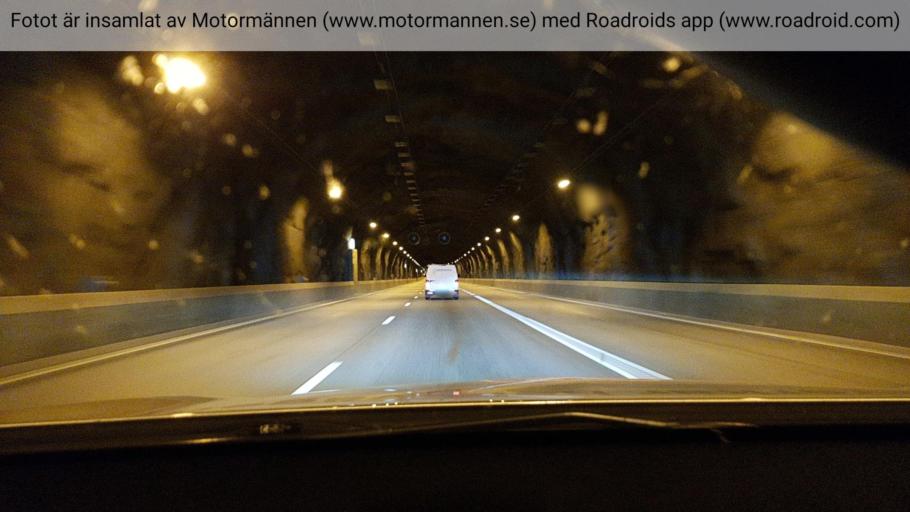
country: SE
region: Stockholm
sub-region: Sollentuna Kommun
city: Sollentuna
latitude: 59.4488
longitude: 17.9452
